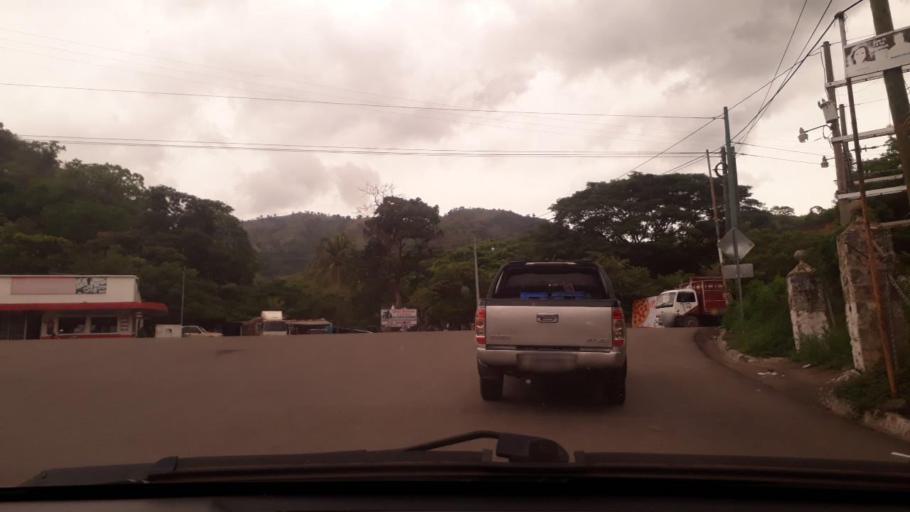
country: GT
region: Chiquimula
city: San Jacinto
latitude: 14.7310
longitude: -89.5052
